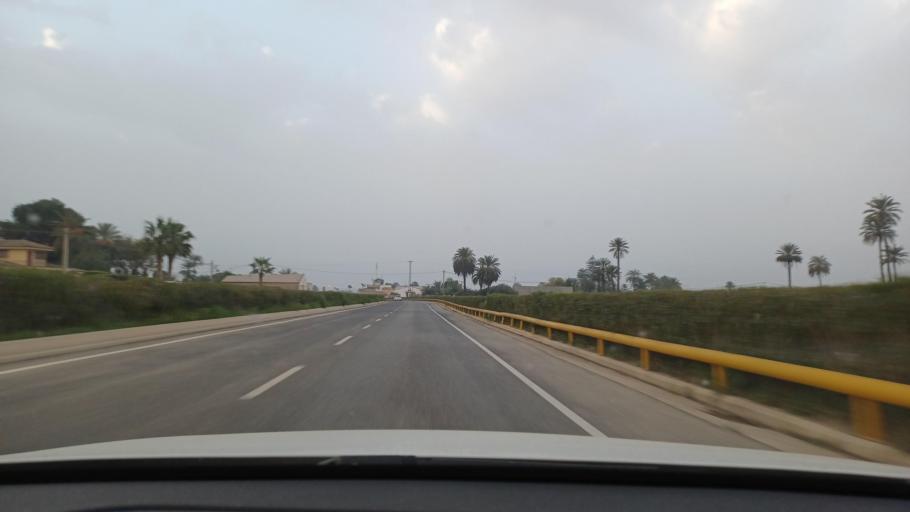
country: ES
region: Valencia
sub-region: Provincia de Alicante
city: Elche
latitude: 38.2273
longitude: -0.6993
